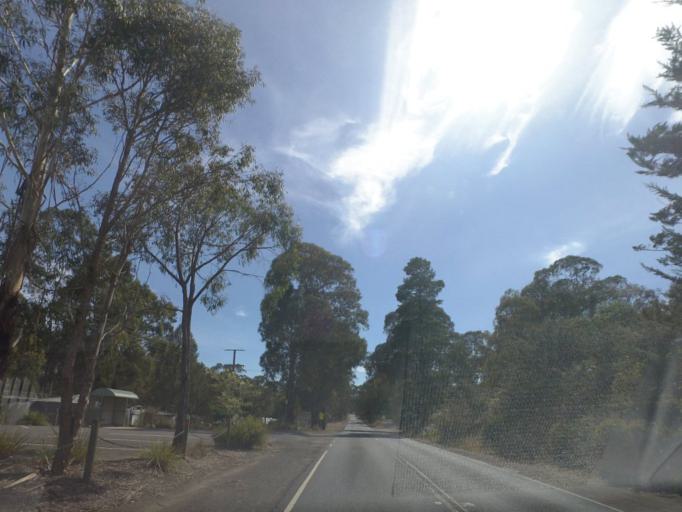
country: AU
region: Victoria
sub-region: Nillumbik
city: Saint Andrews
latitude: -37.6031
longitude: 145.2690
